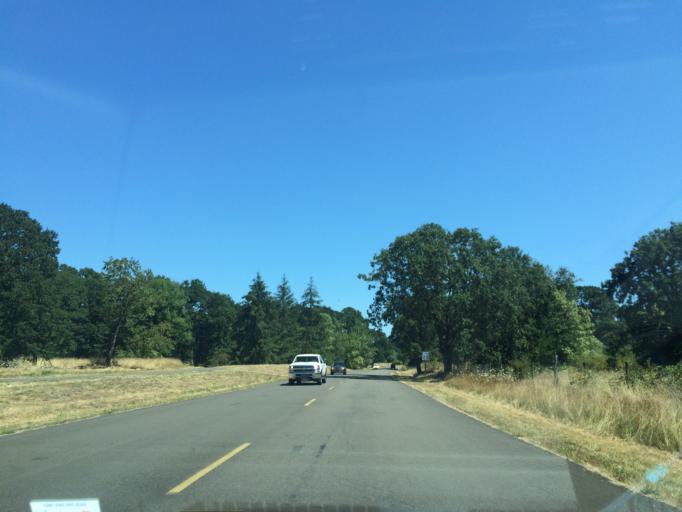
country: US
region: Oregon
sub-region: Yamhill County
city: Newberg
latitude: 45.2496
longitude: -122.8894
